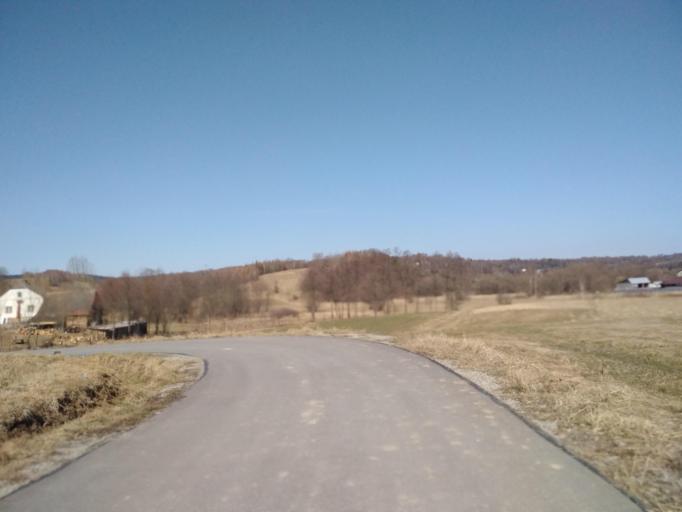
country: PL
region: Subcarpathian Voivodeship
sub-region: Powiat brzozowski
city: Jasienica Rosielna
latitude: 49.7638
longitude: 21.9509
